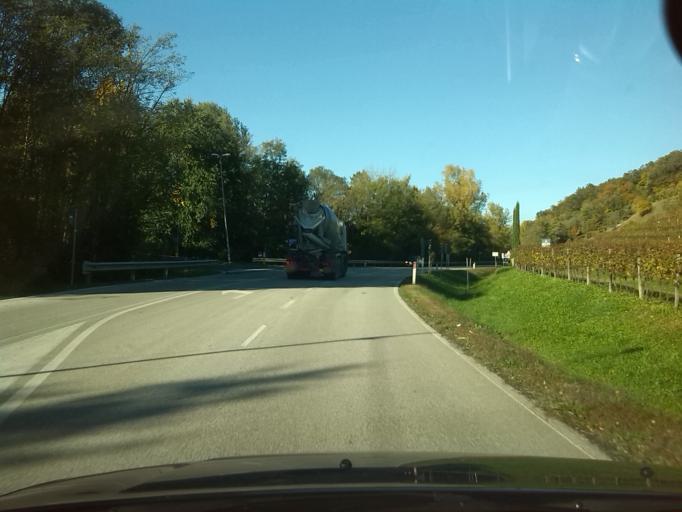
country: IT
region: Friuli Venezia Giulia
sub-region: Provincia di Udine
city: Corno di Rosazzo
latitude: 45.9915
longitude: 13.4675
